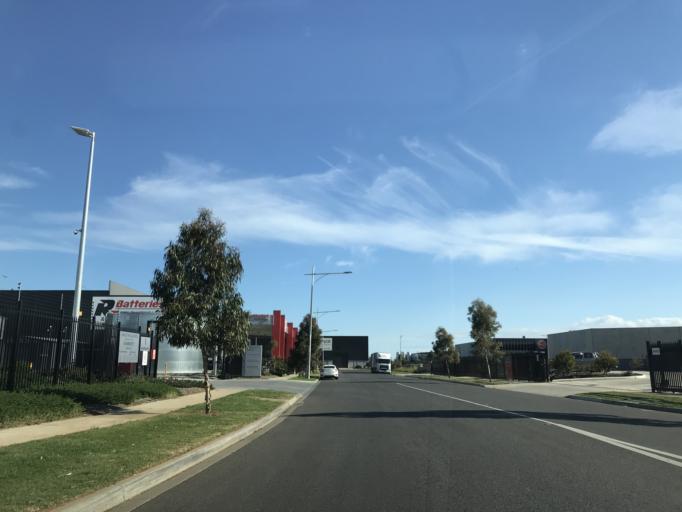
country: AU
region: Victoria
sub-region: Wyndham
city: Truganina
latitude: -37.8123
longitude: 144.7552
